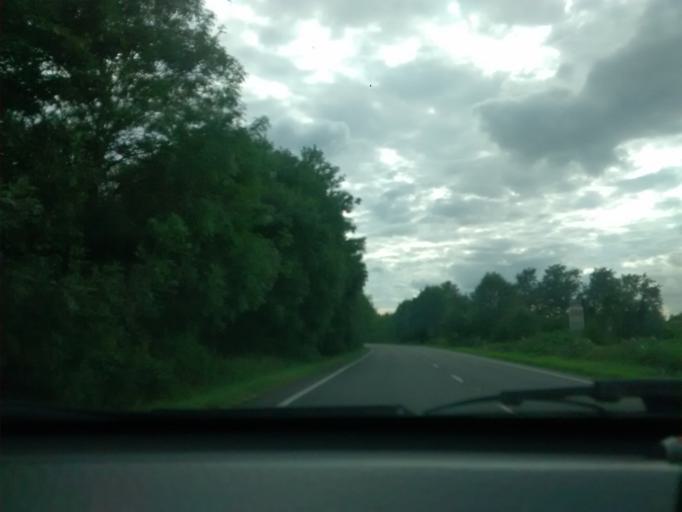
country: GB
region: England
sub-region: Norfolk
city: Downham Market
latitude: 52.5608
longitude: 0.3855
